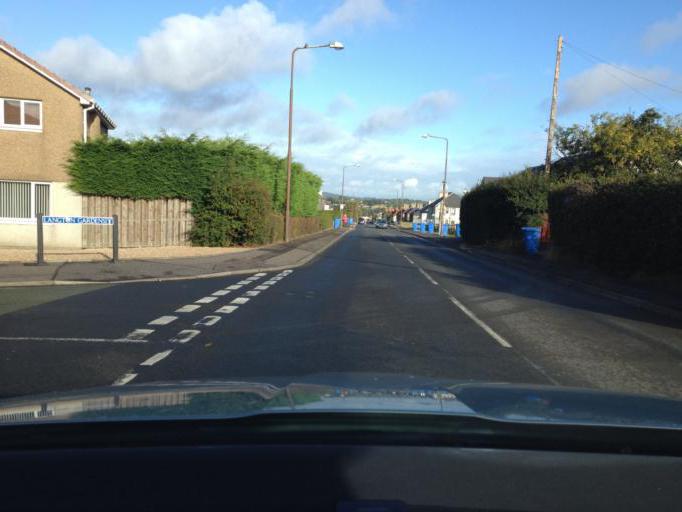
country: GB
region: Scotland
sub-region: West Lothian
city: East Calder
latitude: 55.8896
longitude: -3.4612
